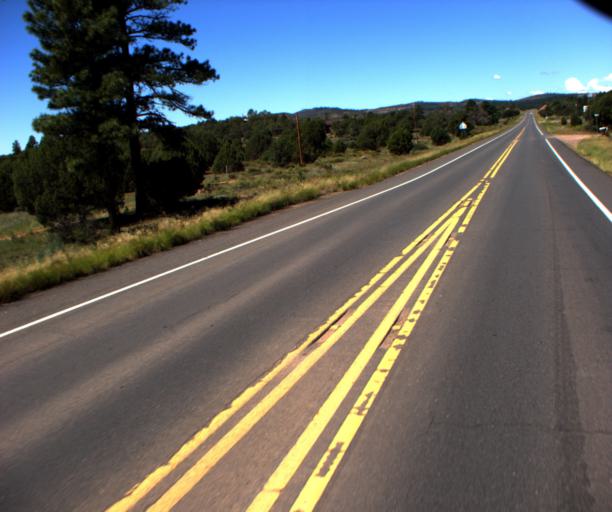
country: US
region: Arizona
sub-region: Navajo County
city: Linden
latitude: 34.2854
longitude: -110.1397
